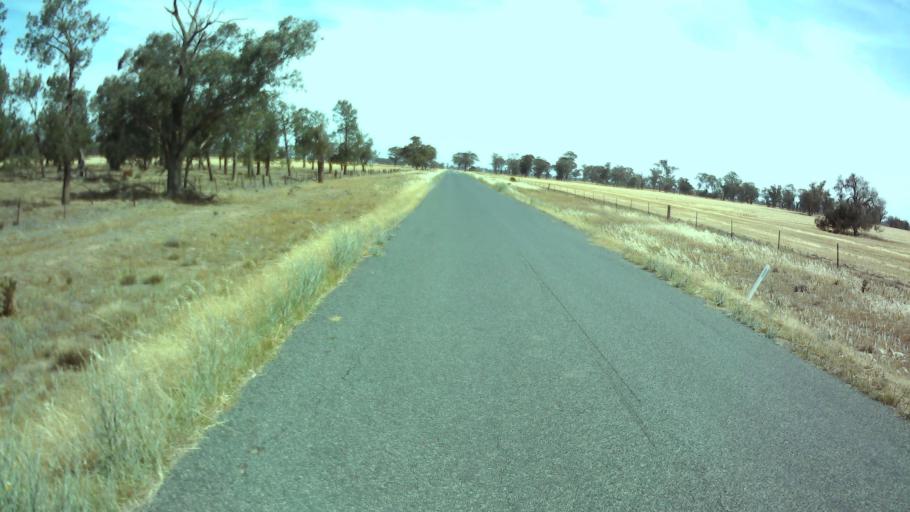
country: AU
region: New South Wales
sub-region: Weddin
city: Grenfell
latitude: -33.9998
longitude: 147.7743
